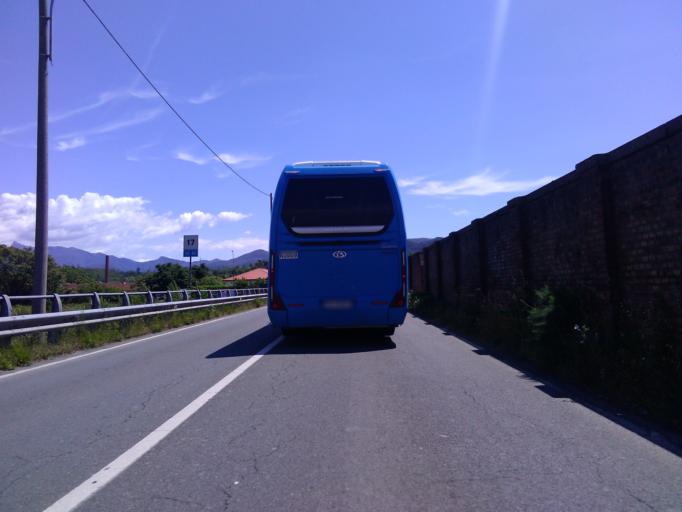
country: IT
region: Tuscany
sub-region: Provincia di Massa-Carrara
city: Terrarossa
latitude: 44.2240
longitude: 9.9693
